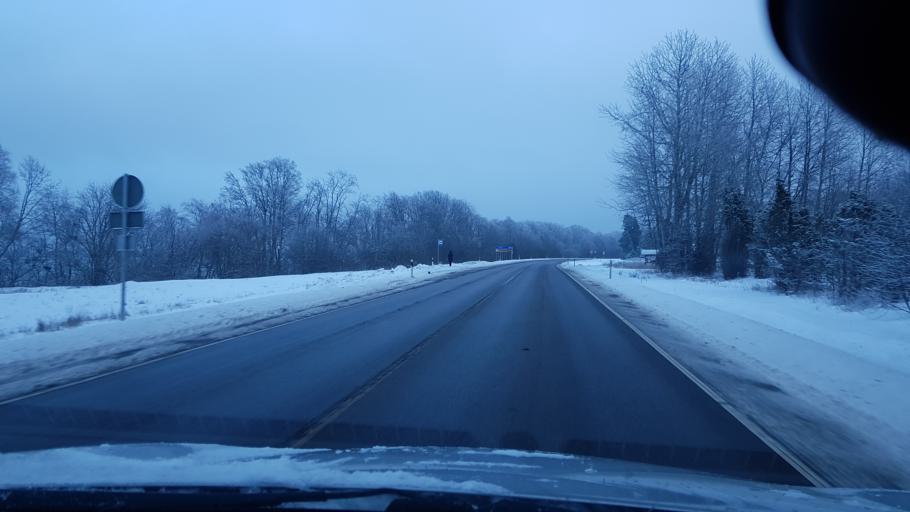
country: EE
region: Harju
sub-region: Paldiski linn
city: Paldiski
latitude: 59.3434
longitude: 24.1923
